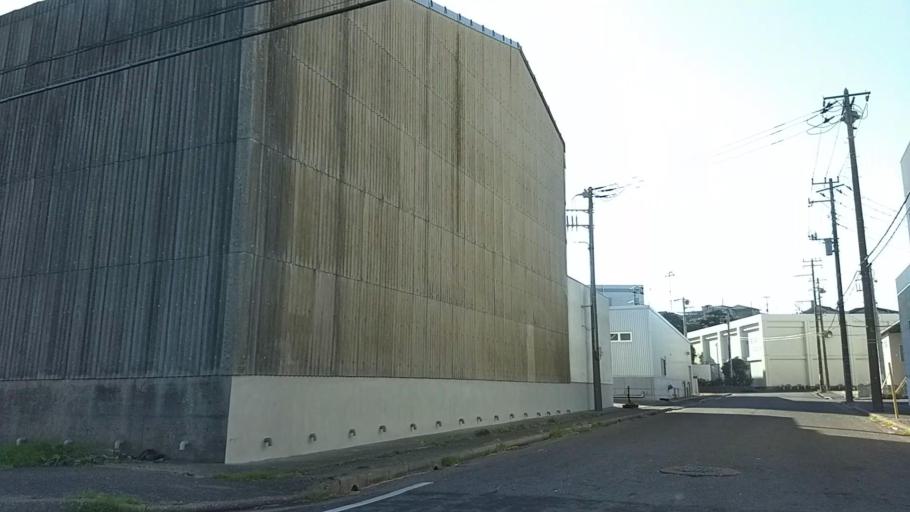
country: JP
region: Chiba
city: Hasaki
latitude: 35.7420
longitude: 140.8625
